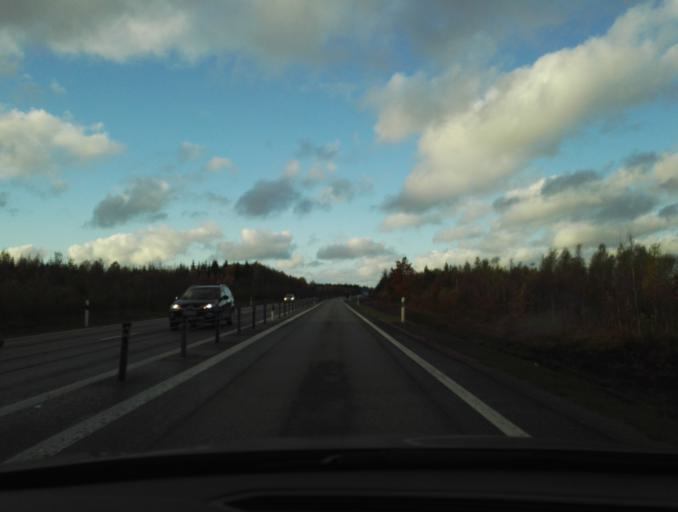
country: SE
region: Kronoberg
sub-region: Vaxjo Kommun
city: Vaexjoe
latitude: 56.9078
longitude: 14.7257
